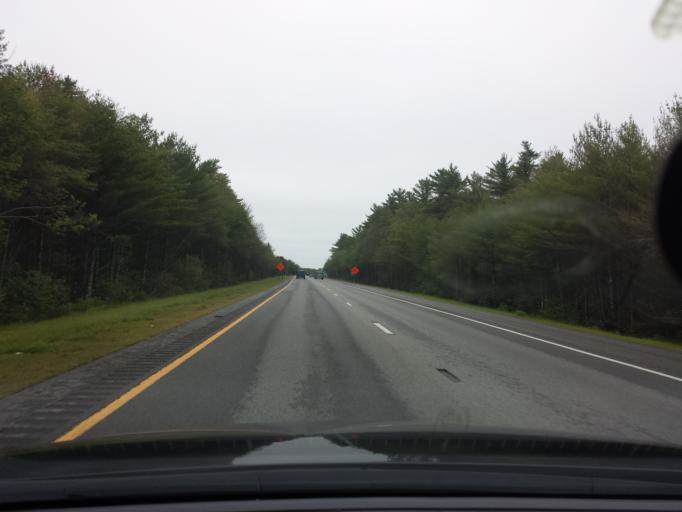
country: US
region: Massachusetts
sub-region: Plymouth County
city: Marion Center
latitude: 41.7175
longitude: -70.7833
